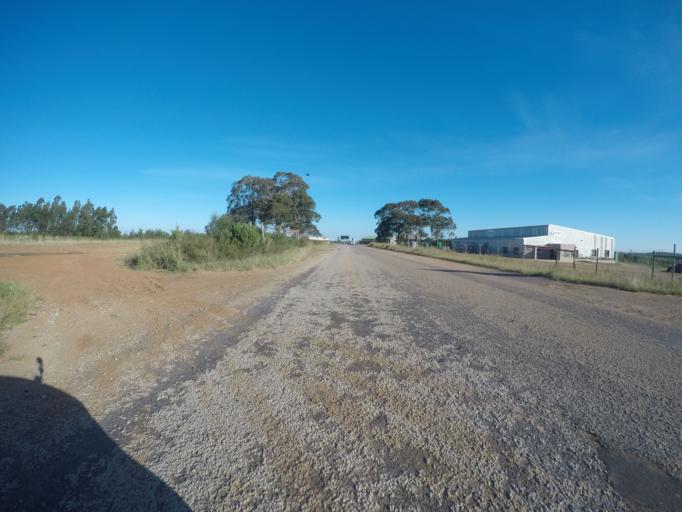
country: ZA
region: Eastern Cape
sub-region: Cacadu District Municipality
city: Kareedouw
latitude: -34.0038
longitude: 24.2342
